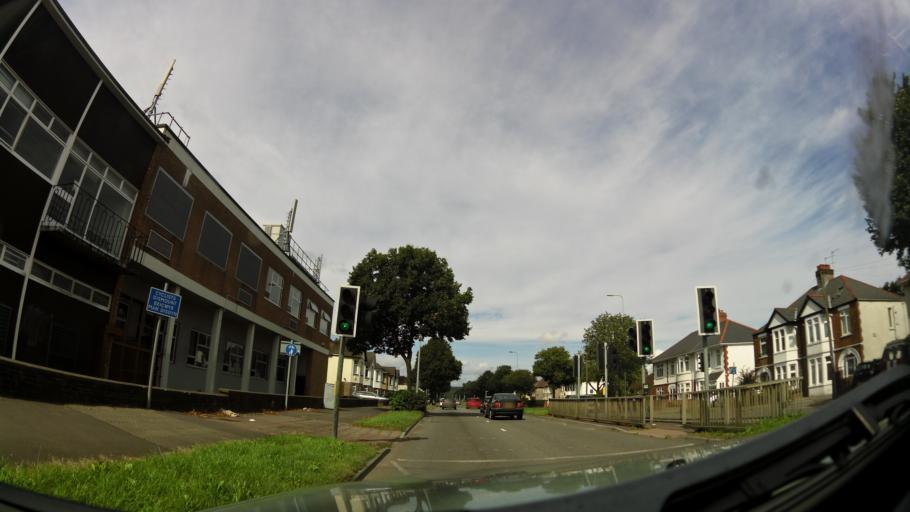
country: GB
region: Wales
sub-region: Cardiff
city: Cardiff
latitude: 51.5116
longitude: -3.2058
